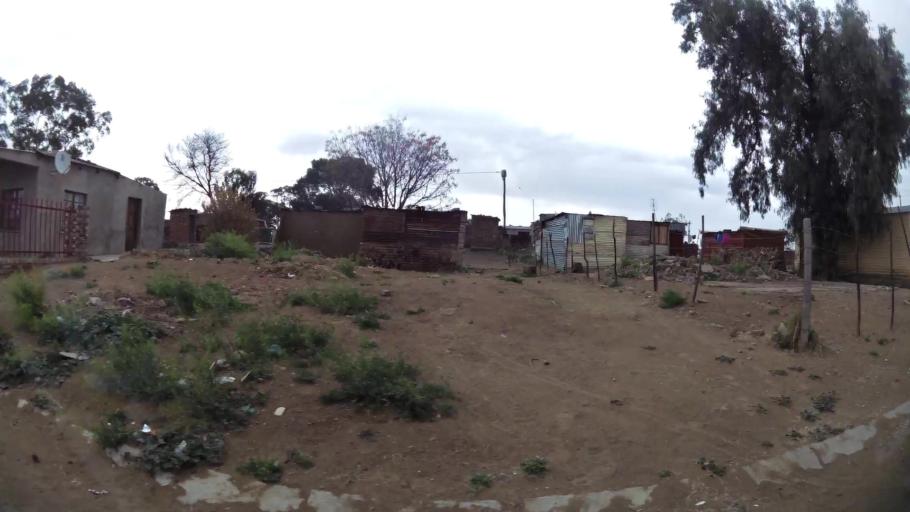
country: ZA
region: Orange Free State
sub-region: Fezile Dabi District Municipality
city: Kroonstad
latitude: -27.6462
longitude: 27.2180
